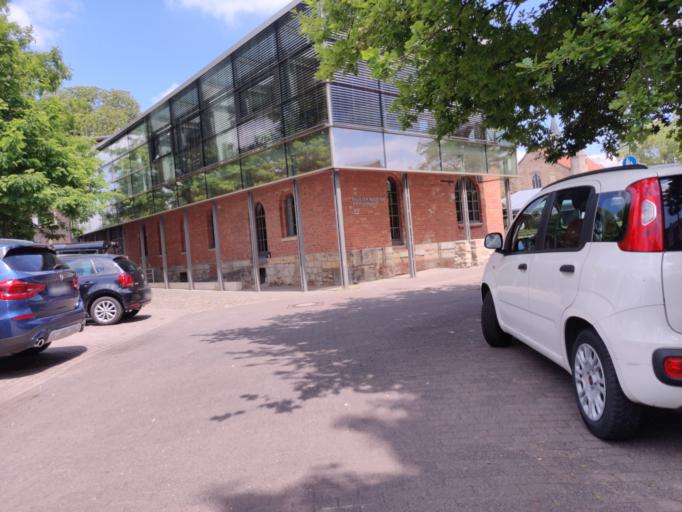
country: DE
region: Lower Saxony
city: Hildesheim
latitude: 52.1498
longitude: 9.9404
